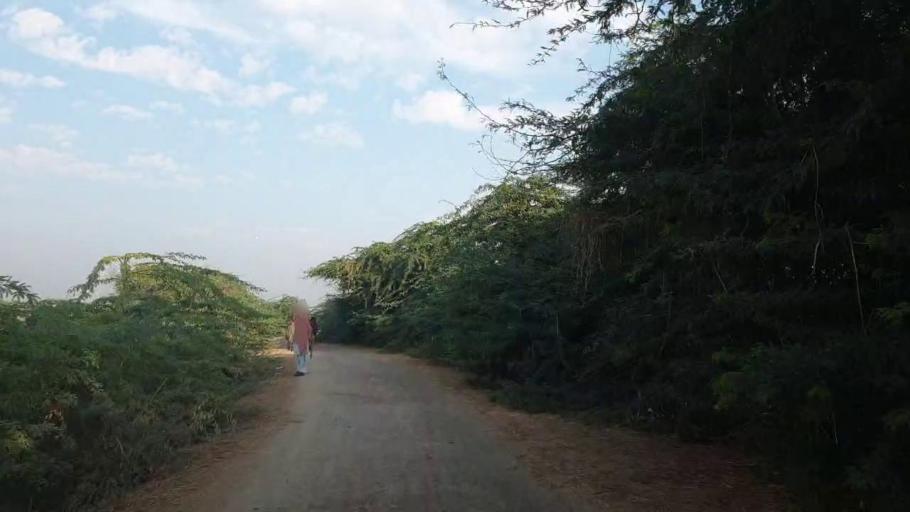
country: PK
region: Sindh
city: Tando Bago
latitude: 24.8094
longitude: 68.9573
